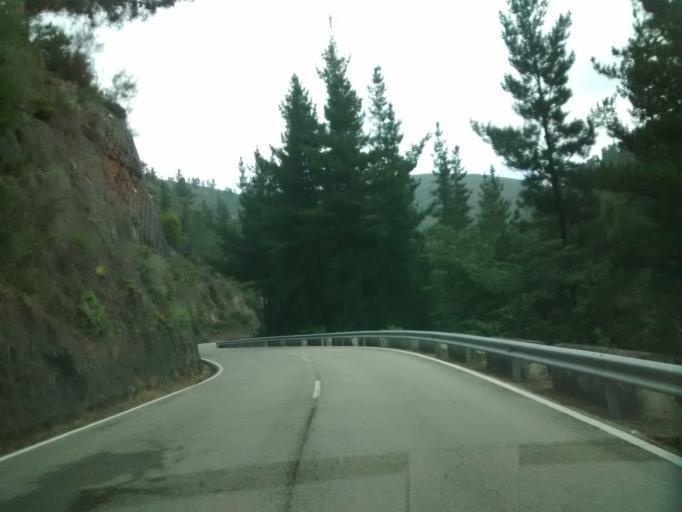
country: ES
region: Galicia
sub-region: Provincia de Ourense
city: Manzaneda
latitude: 42.3384
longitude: -7.2038
